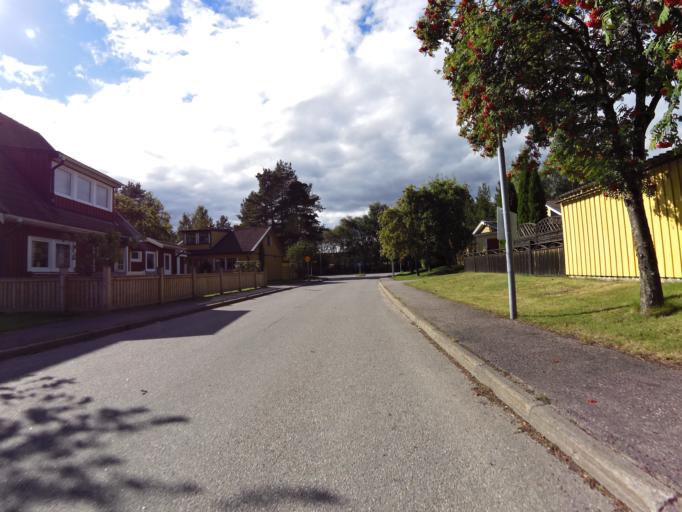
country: SE
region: Gaevleborg
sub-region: Gavle Kommun
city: Gavle
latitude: 60.6673
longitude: 17.2173
